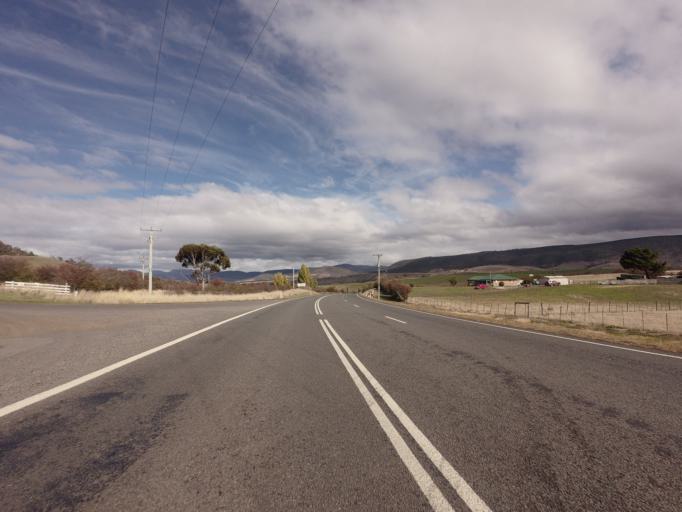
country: AU
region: Tasmania
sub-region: Derwent Valley
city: New Norfolk
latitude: -42.7176
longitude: 146.9480
